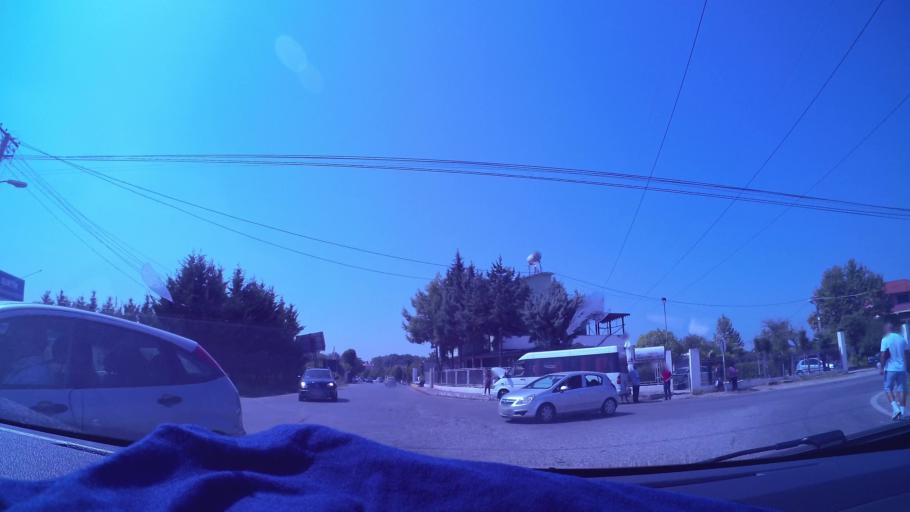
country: AL
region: Durres
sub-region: Rrethi i Durresit
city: Xhafzotaj
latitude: 41.3641
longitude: 19.5505
